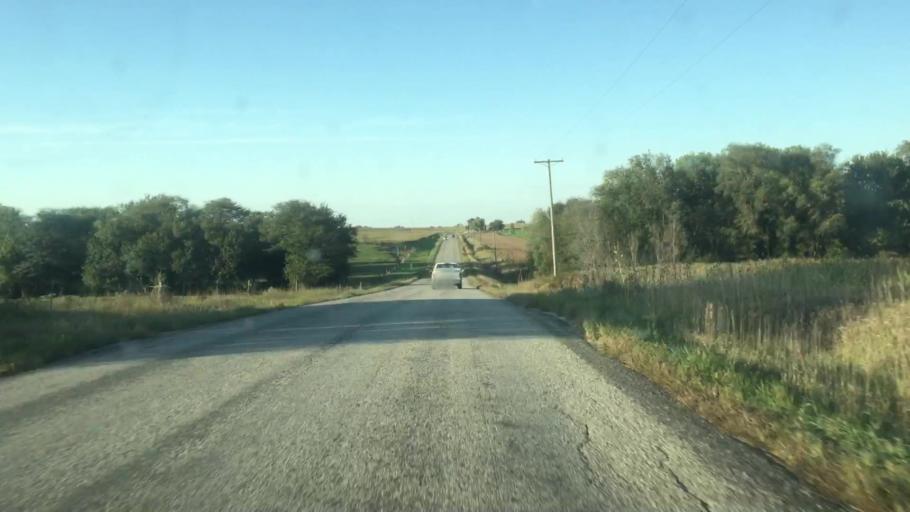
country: US
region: Kansas
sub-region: Brown County
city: Horton
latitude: 39.5584
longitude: -95.4021
